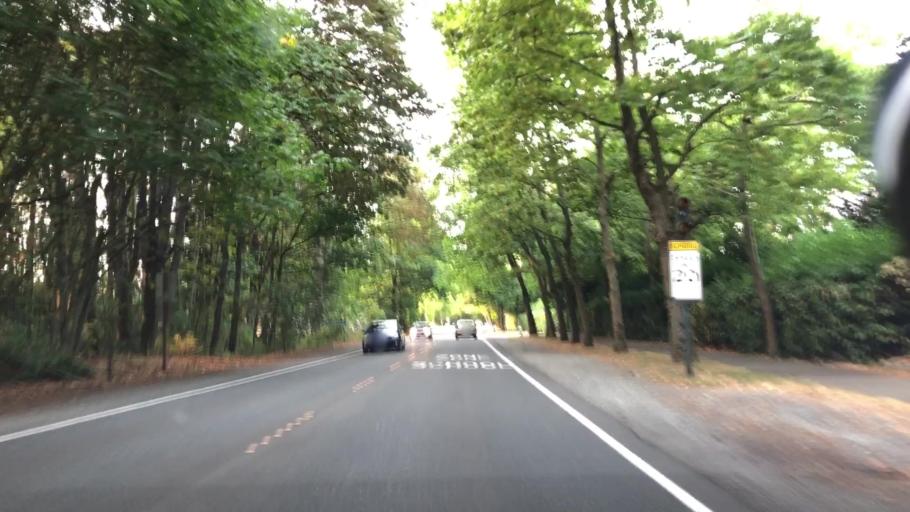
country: US
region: Washington
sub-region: King County
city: Mercer Island
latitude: 47.5520
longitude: -122.2216
